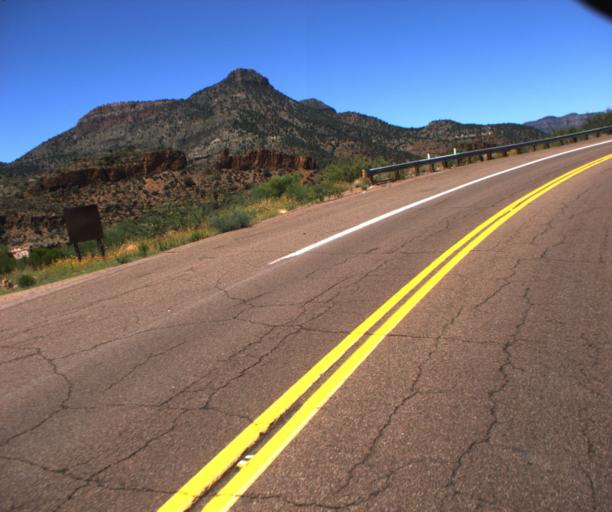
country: US
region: Arizona
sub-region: Navajo County
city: Cibecue
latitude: 33.7989
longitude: -110.5065
